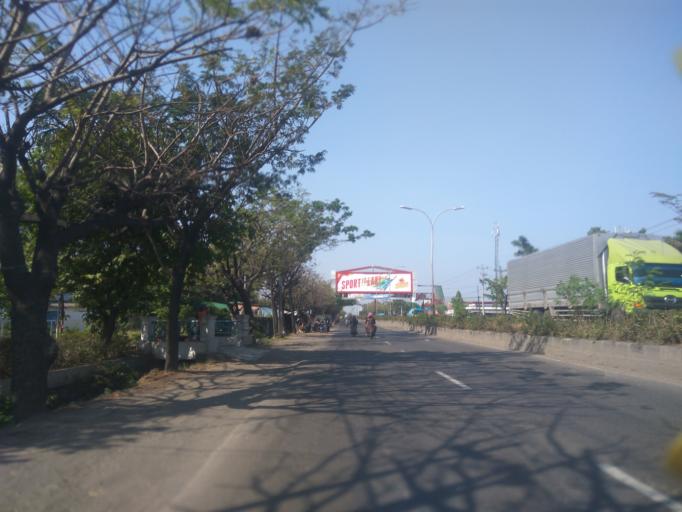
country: ID
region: Central Java
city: Semarang
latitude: -6.9480
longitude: 110.4894
